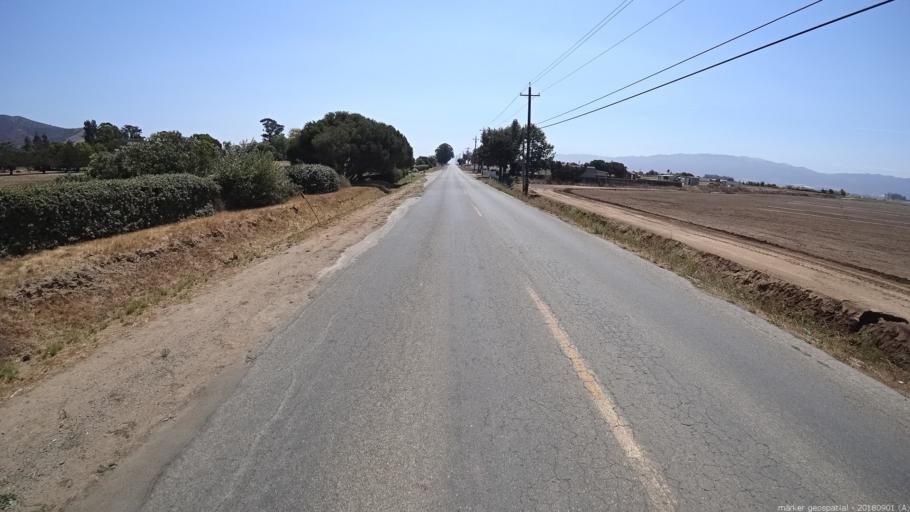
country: US
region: California
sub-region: Monterey County
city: Salinas
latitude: 36.6705
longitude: -121.5523
